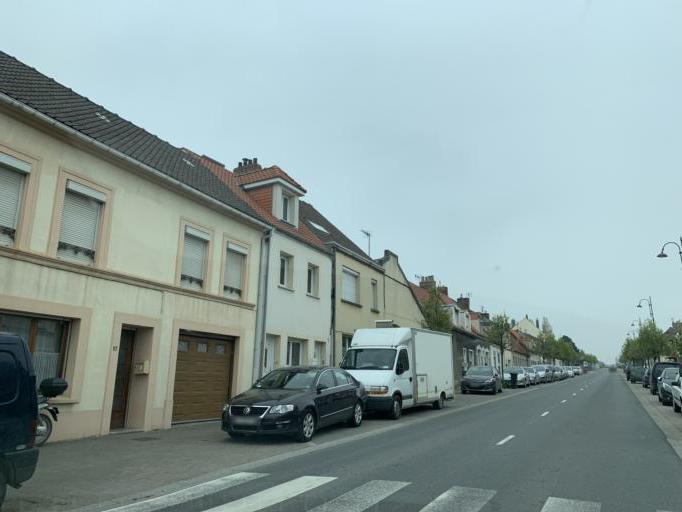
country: FR
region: Nord-Pas-de-Calais
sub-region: Departement du Pas-de-Calais
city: Marquise
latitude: 50.8168
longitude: 1.7028
